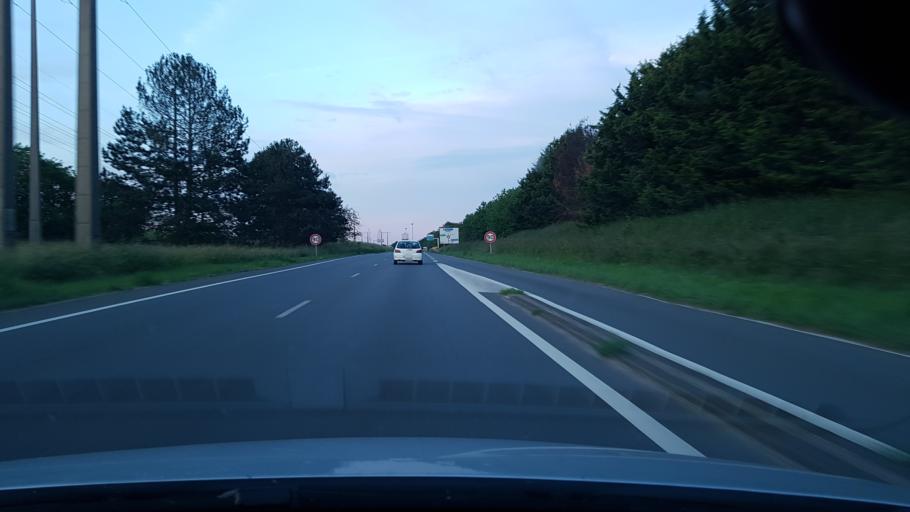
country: FR
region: Ile-de-France
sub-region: Departement de l'Essonne
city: Les Ulis
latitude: 48.6747
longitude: 2.1809
